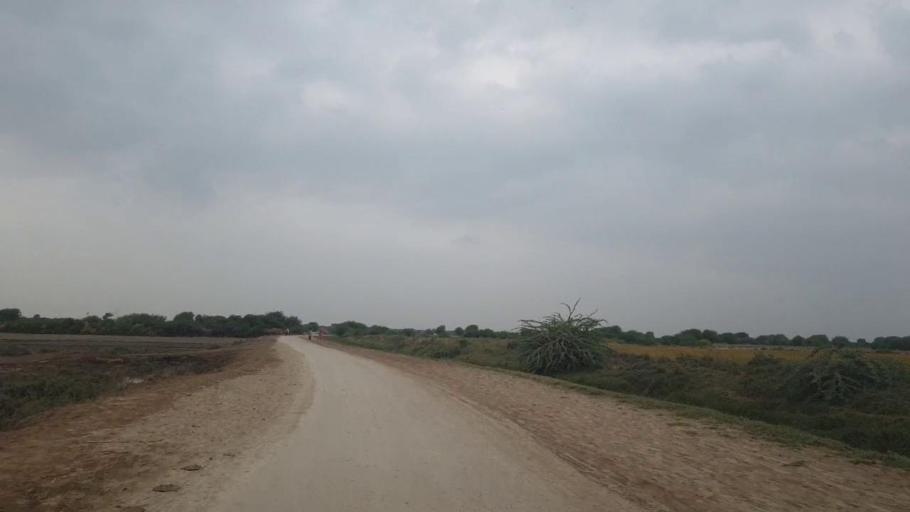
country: PK
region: Sindh
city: Badin
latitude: 24.6419
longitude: 68.6815
